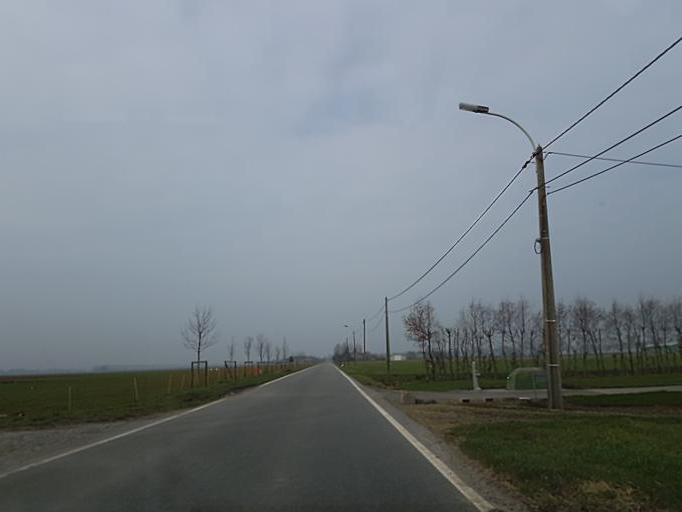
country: BE
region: Flanders
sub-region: Provincie Oost-Vlaanderen
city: Beveren
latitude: 51.3039
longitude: 4.2044
